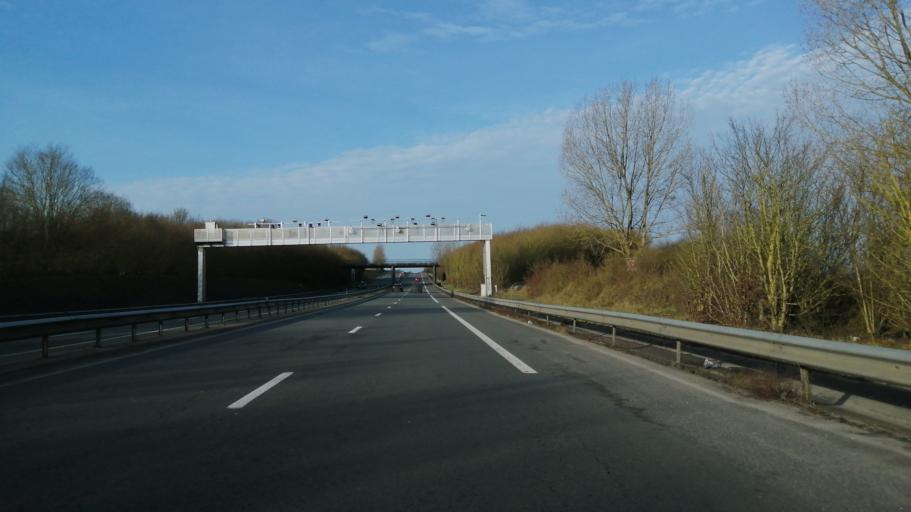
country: FR
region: Nord-Pas-de-Calais
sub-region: Departement du Pas-de-Calais
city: Rety
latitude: 50.7387
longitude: 1.7888
